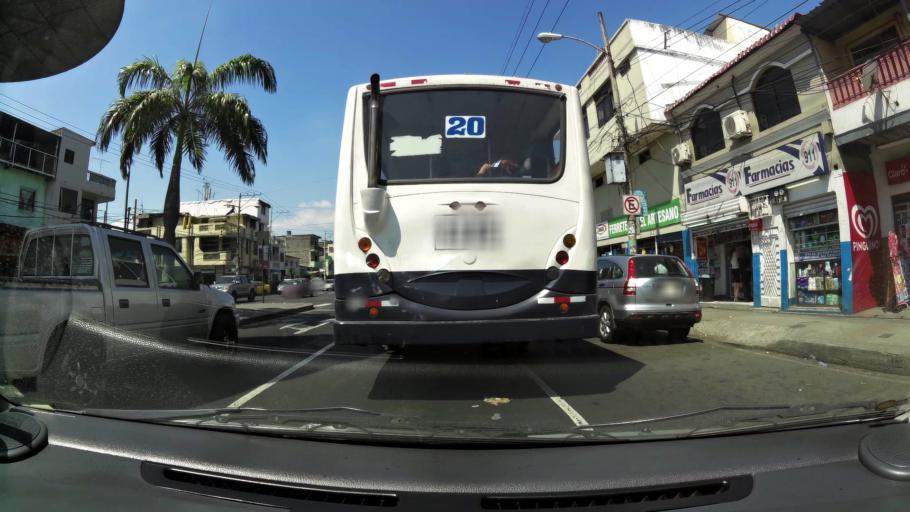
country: EC
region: Guayas
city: Guayaquil
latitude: -2.1993
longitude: -79.9260
